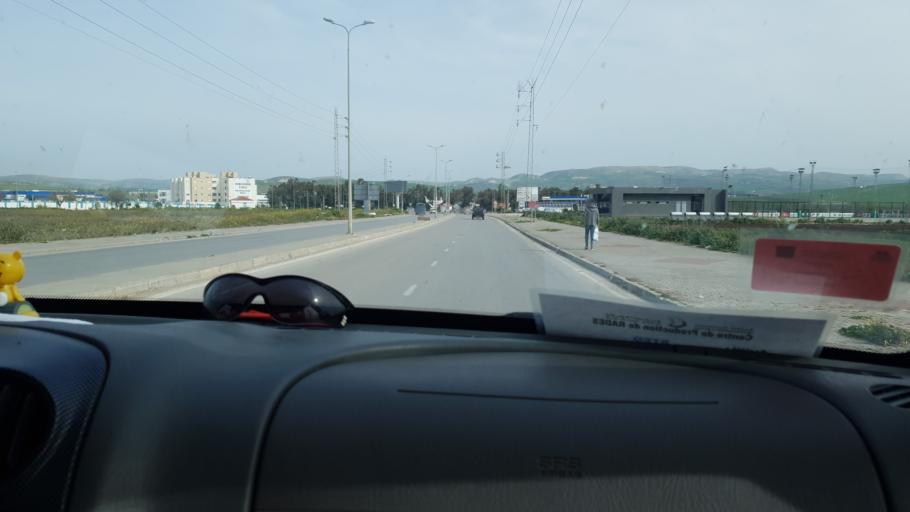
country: TN
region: Bajah
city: Beja
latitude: 36.7275
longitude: 9.2061
